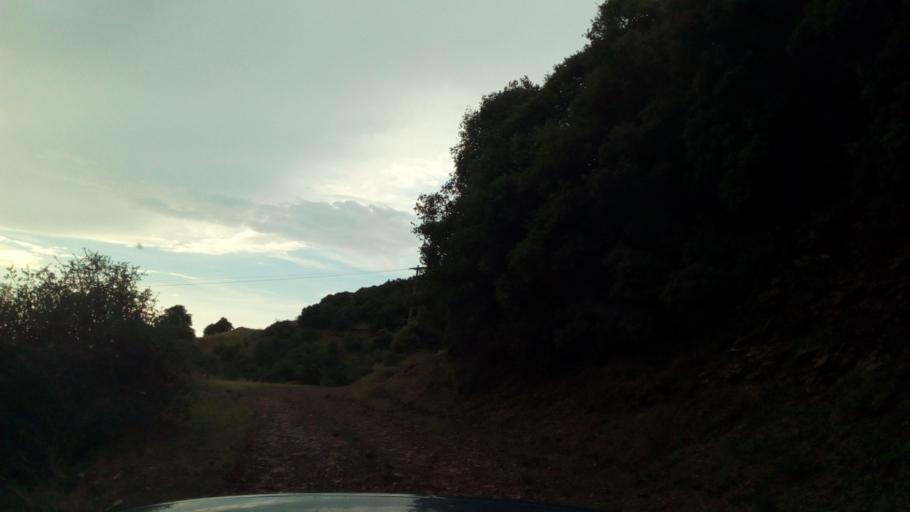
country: GR
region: West Greece
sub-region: Nomos Achaias
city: Kamarai
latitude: 38.4153
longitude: 22.0476
